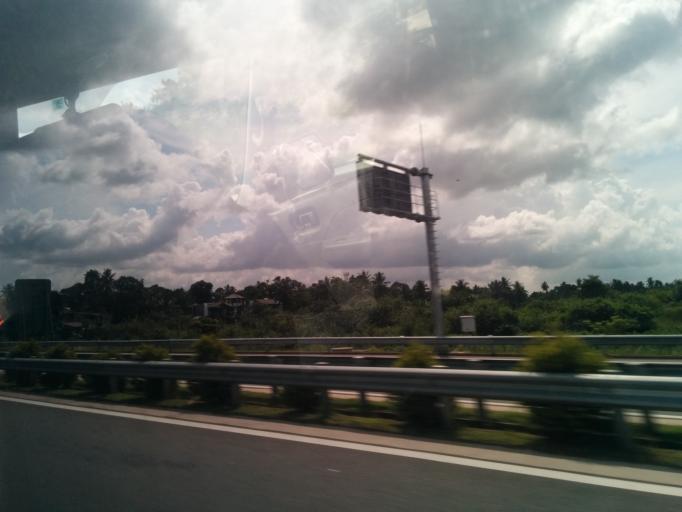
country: LK
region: Western
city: Wattala
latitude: 6.9720
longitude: 79.8940
